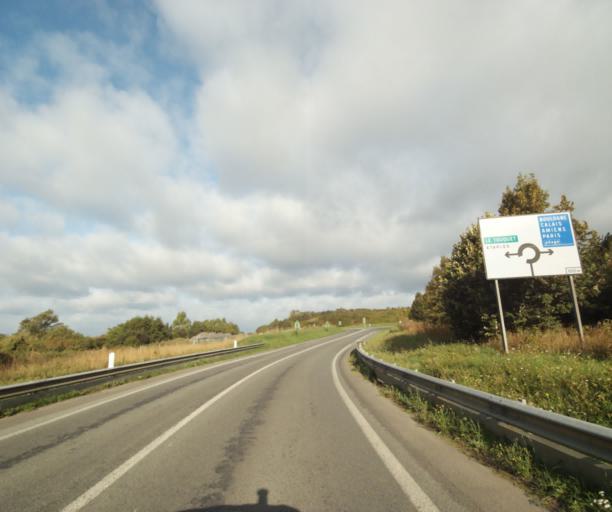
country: FR
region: Nord-Pas-de-Calais
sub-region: Departement du Pas-de-Calais
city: Saint-Josse
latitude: 50.5035
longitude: 1.6806
